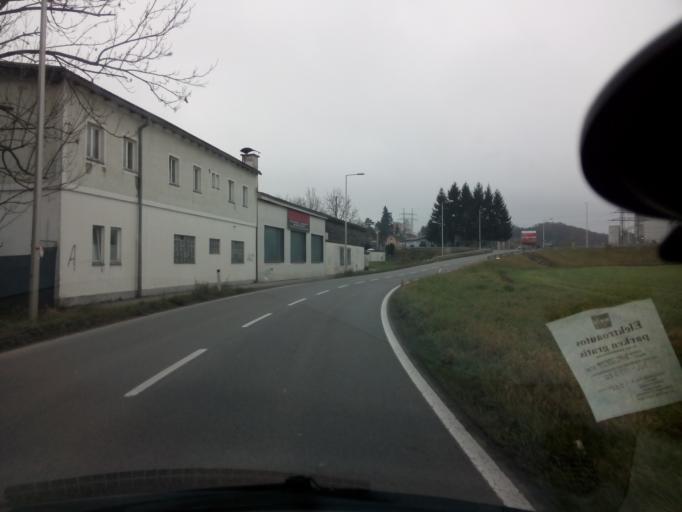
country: AT
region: Upper Austria
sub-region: Politischer Bezirk Gmunden
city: Gmunden
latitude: 47.9294
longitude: 13.7858
